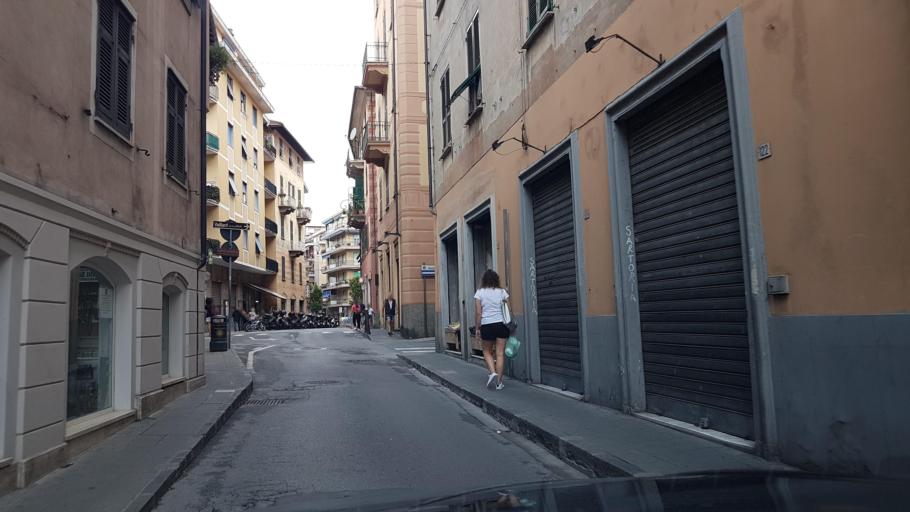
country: IT
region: Liguria
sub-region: Provincia di Genova
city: Rapallo
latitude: 44.3514
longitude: 9.2264
